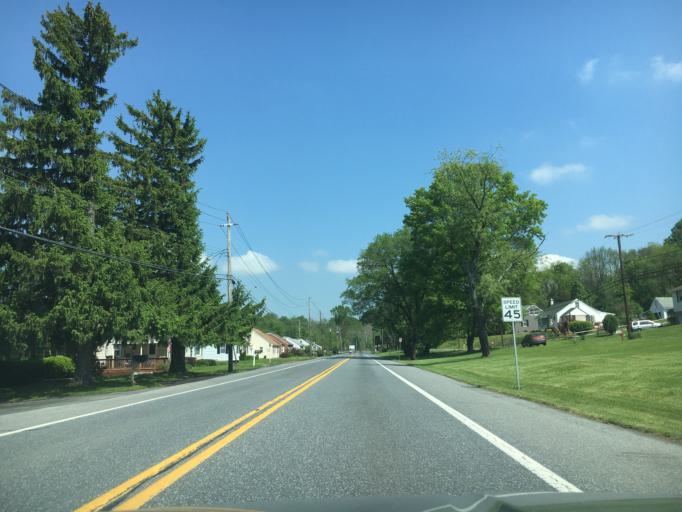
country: US
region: Pennsylvania
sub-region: Berks County
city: Boyertown
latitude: 40.3458
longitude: -75.6607
